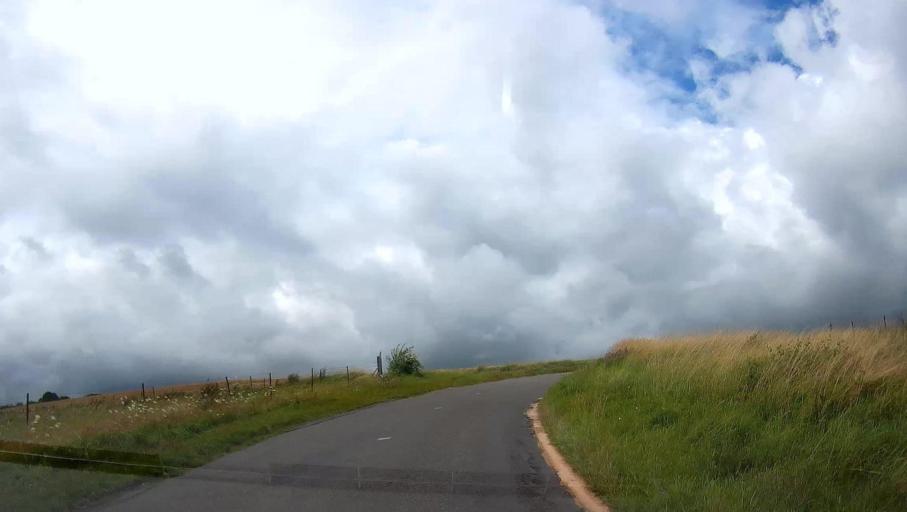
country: FR
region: Champagne-Ardenne
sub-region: Departement des Ardennes
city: Tournes
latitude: 49.7449
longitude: 4.5891
